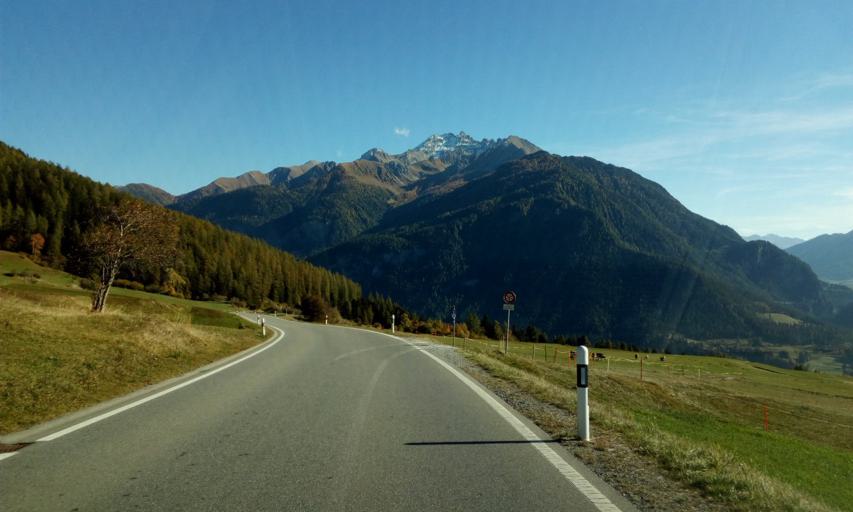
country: CH
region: Grisons
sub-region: Albula District
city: Tiefencastel
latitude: 46.6787
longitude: 9.5707
